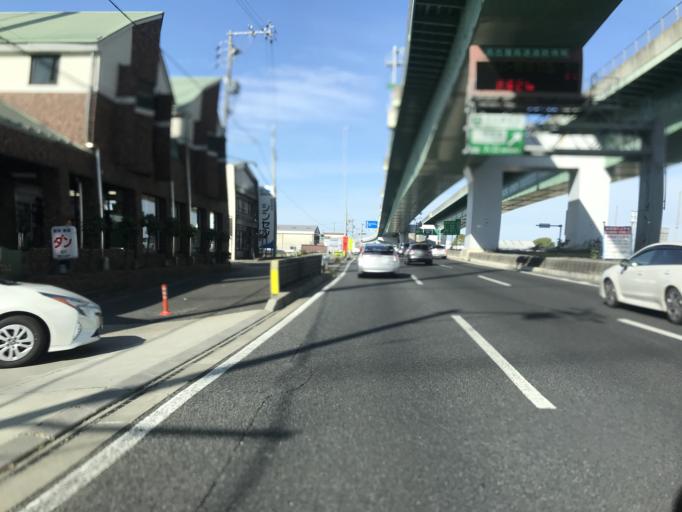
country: JP
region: Aichi
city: Iwakura
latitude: 35.2577
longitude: 136.8423
